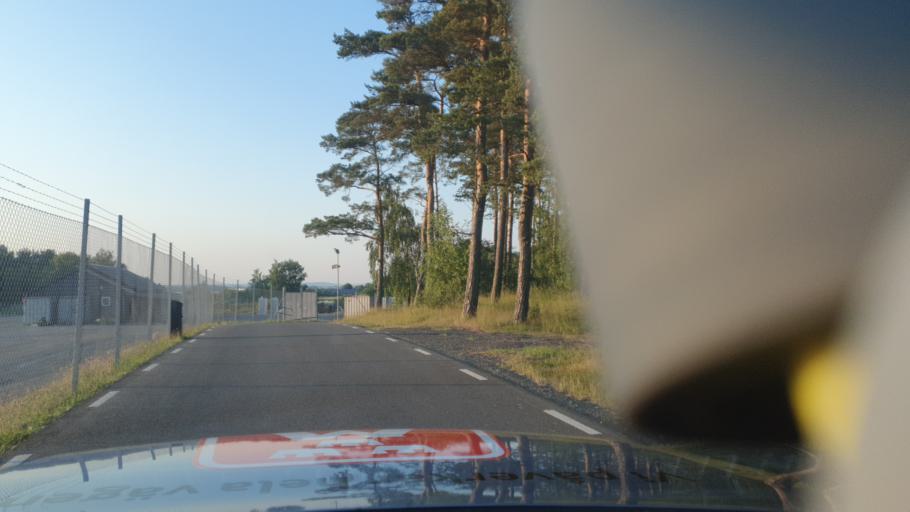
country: SE
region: Skane
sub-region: Kristianstads Kommun
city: Norra Asum
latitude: 55.9862
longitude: 14.1244
